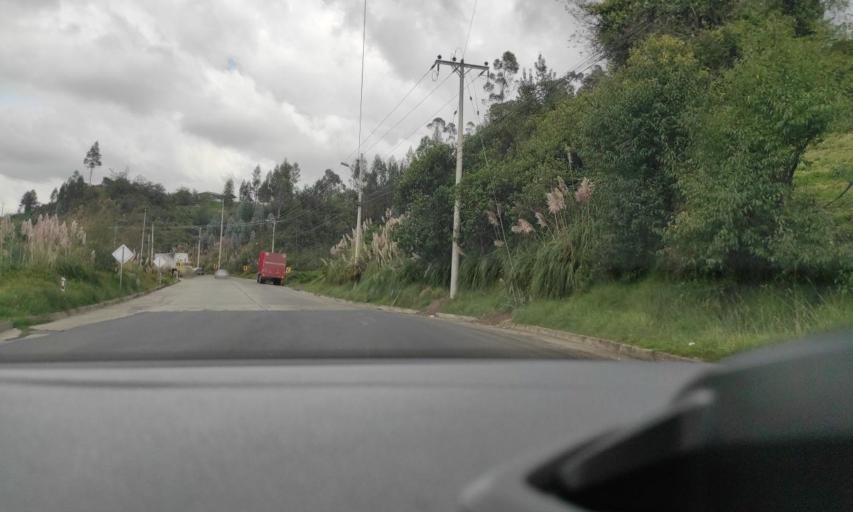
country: EC
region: Canar
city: Azogues
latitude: -2.6901
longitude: -78.8897
